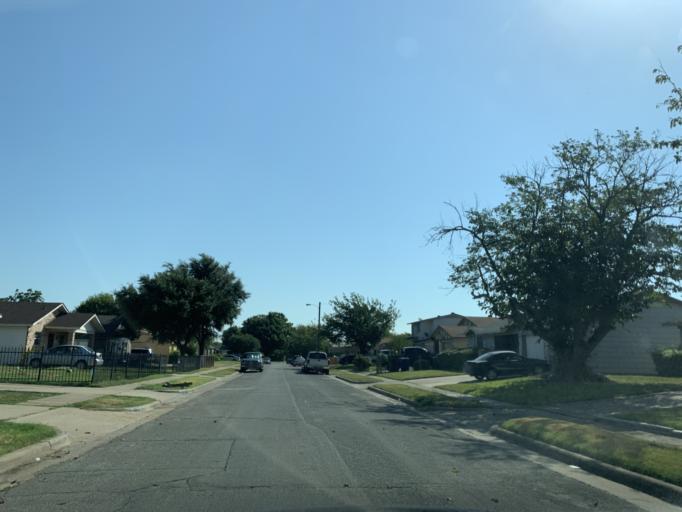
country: US
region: Texas
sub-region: Dallas County
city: Hutchins
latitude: 32.6681
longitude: -96.7630
